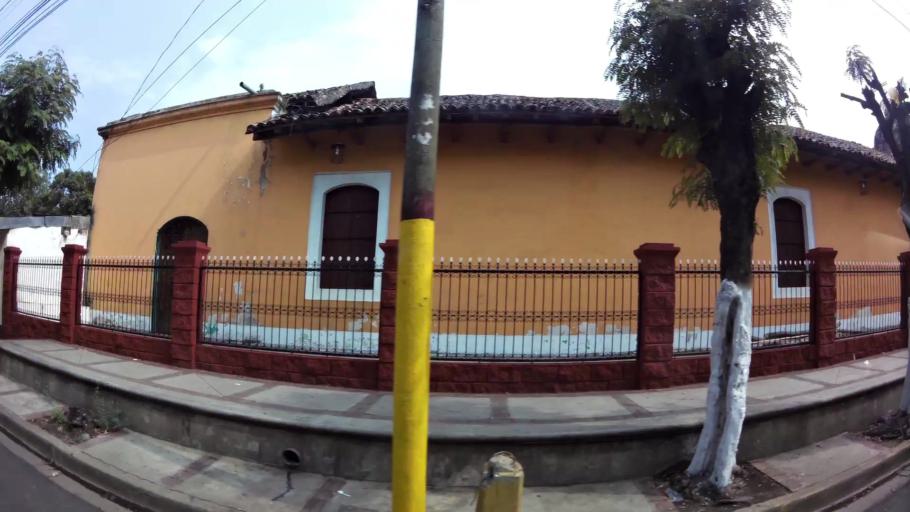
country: NI
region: Masaya
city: Masaya
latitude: 11.9741
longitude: -86.0993
